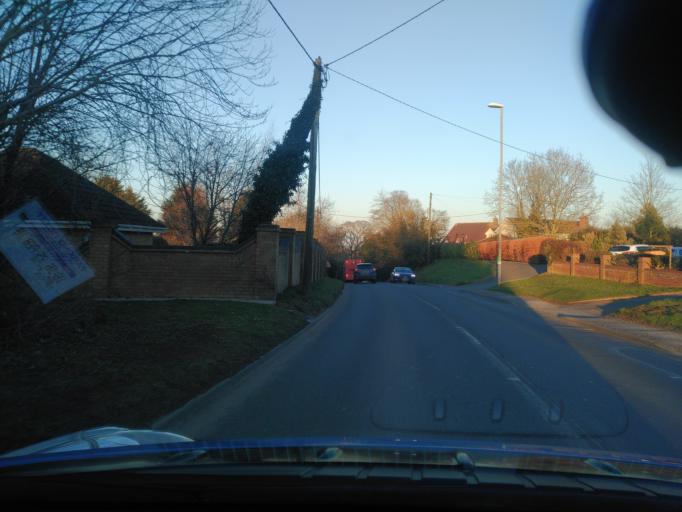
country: GB
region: England
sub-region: Central Bedfordshire
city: Toddington
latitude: 51.9519
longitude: -0.5257
